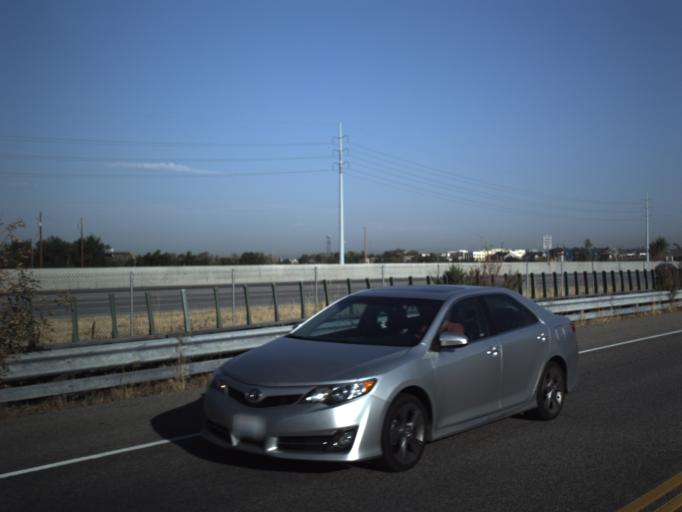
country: US
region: Utah
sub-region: Davis County
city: Farmington
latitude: 40.9755
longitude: -111.8945
